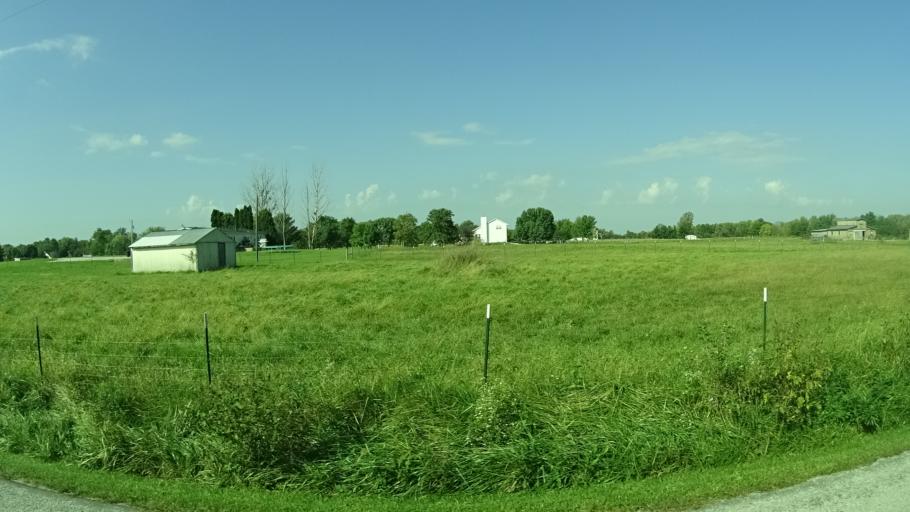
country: US
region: Indiana
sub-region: Madison County
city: Lapel
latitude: 40.0239
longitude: -85.8624
